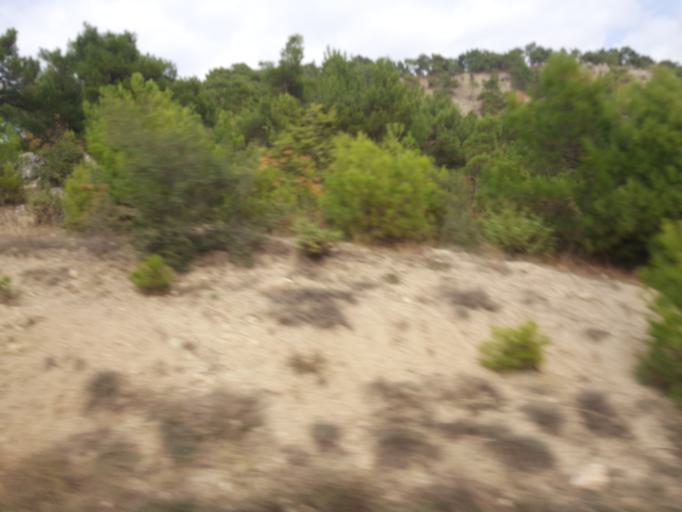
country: TR
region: Sinop
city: Duragan
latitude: 41.4513
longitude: 35.0450
